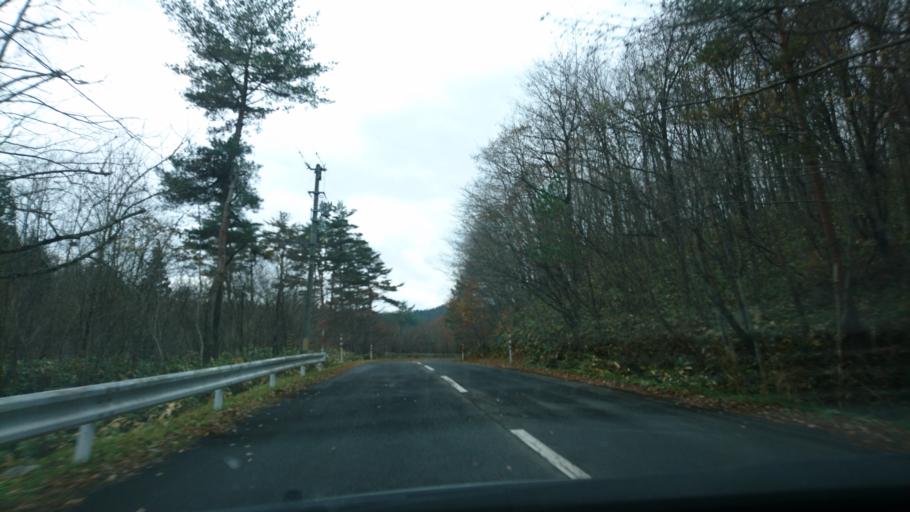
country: JP
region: Iwate
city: Ichinoseki
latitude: 38.9250
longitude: 140.9213
